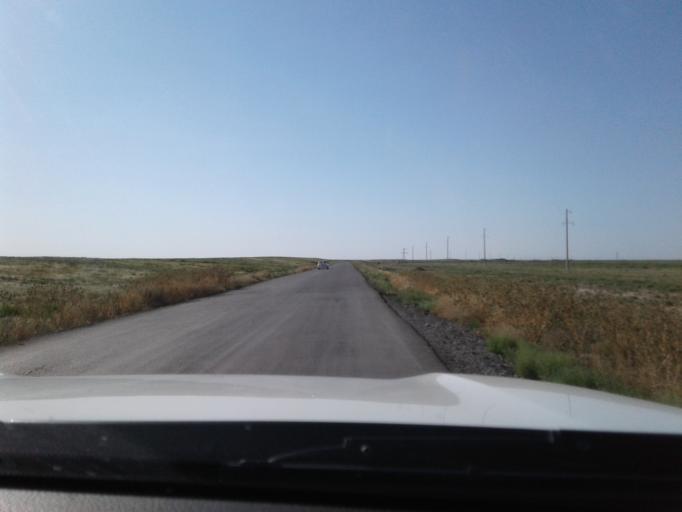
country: IR
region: Razavi Khorasan
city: Kalat-e Naderi
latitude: 37.1550
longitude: 60.0556
